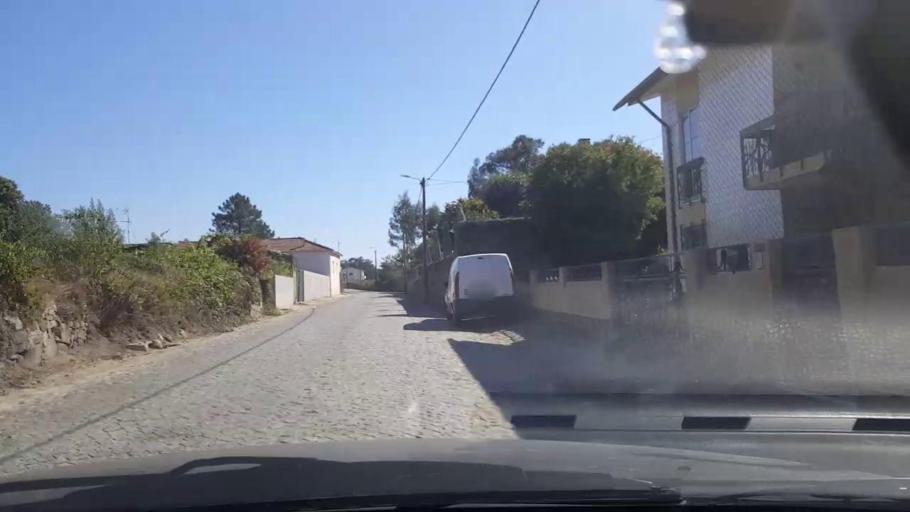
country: PT
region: Porto
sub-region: Vila do Conde
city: Arvore
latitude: 41.3206
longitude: -8.6996
